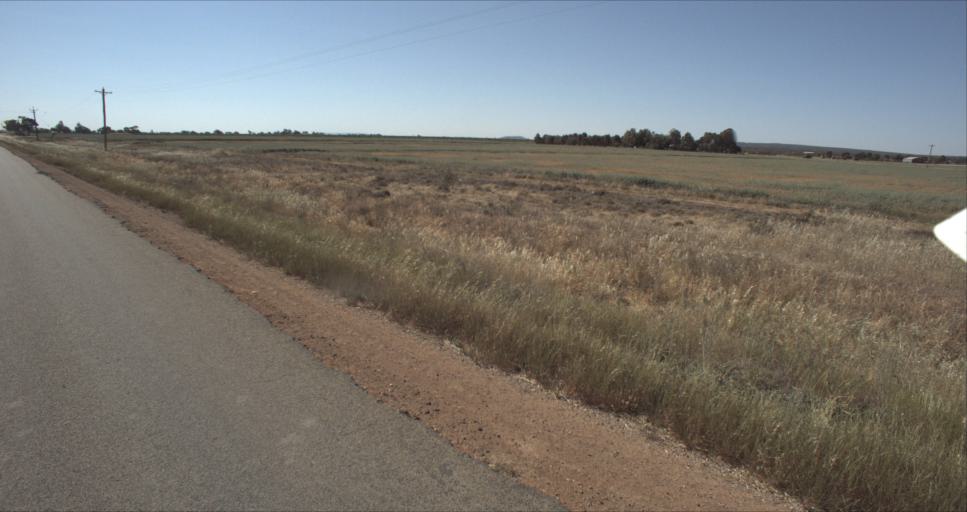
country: AU
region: New South Wales
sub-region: Leeton
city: Leeton
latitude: -34.4861
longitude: 146.3774
